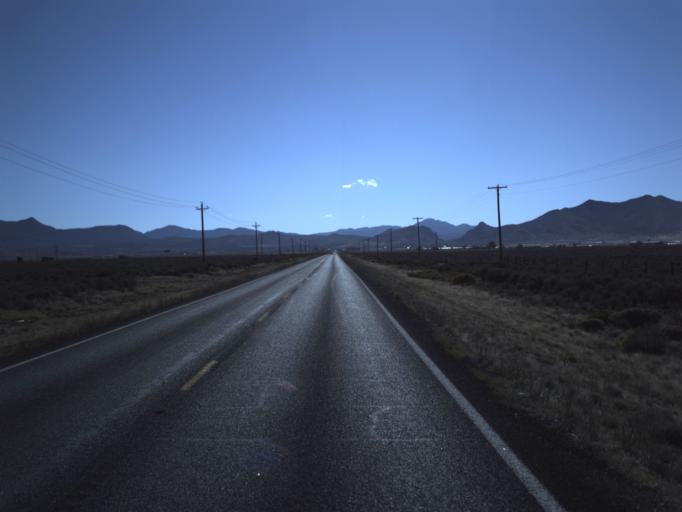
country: US
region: Utah
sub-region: Washington County
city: Enterprise
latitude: 37.6918
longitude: -113.6072
